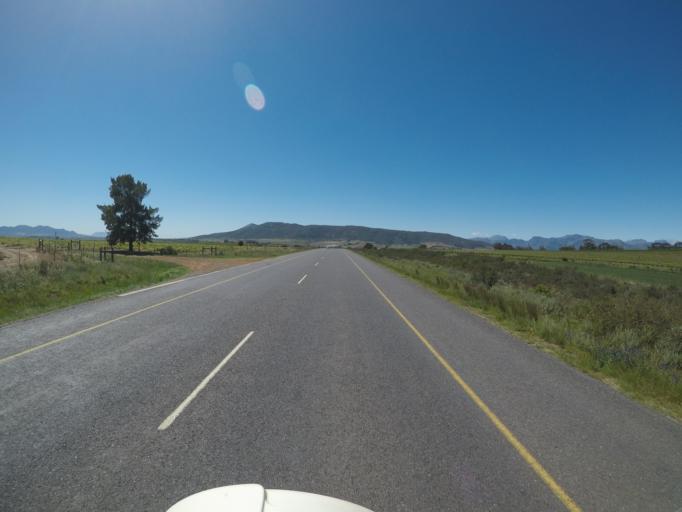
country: ZA
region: Western Cape
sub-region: Cape Winelands District Municipality
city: Paarl
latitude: -33.7861
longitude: 18.8759
